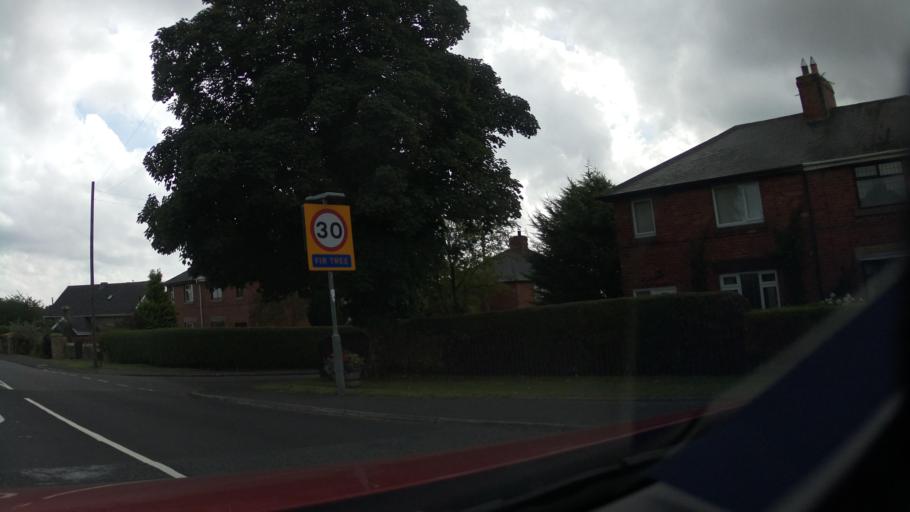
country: GB
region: England
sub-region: County Durham
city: Hamsterley
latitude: 54.7066
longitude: -1.7860
